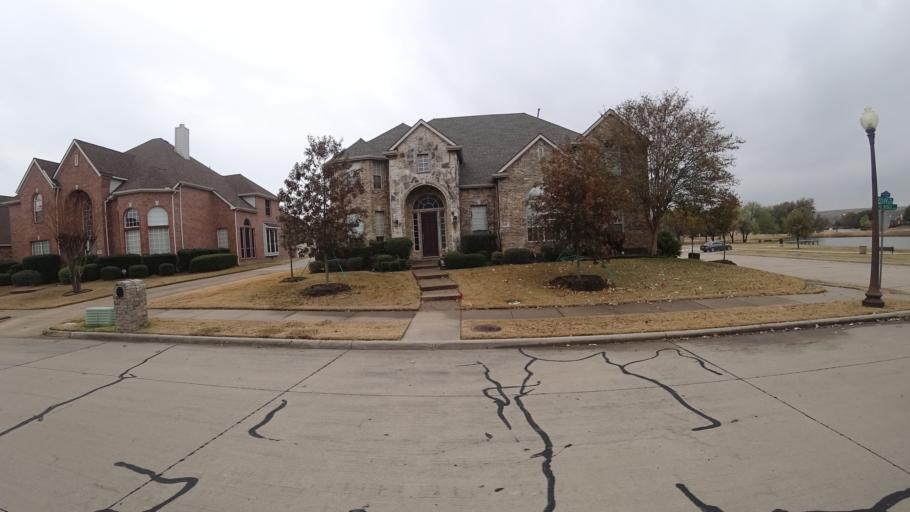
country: US
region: Texas
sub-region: Denton County
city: Lewisville
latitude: 33.0304
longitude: -96.9374
